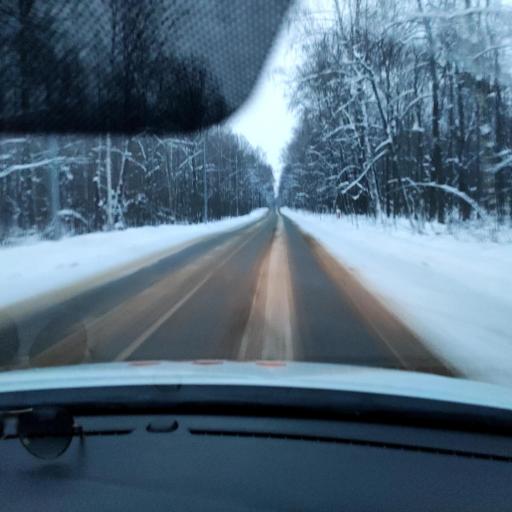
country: RU
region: Tatarstan
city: Vysokaya Gora
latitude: 55.9348
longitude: 49.1771
